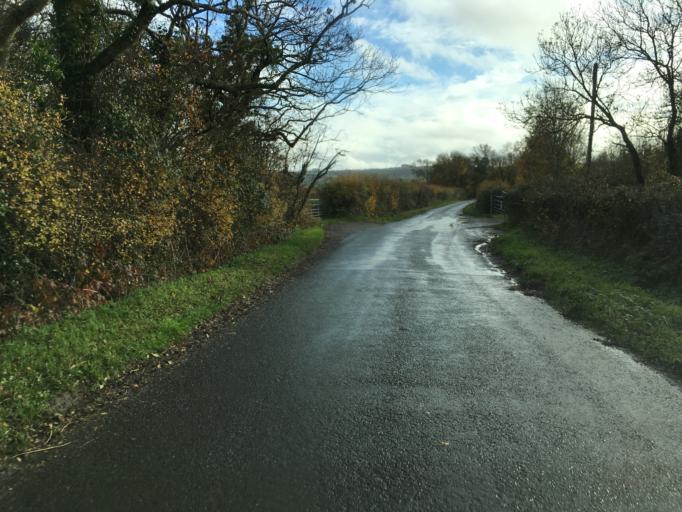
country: GB
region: England
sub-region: South Gloucestershire
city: Pucklechurch
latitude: 51.4824
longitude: -2.4093
